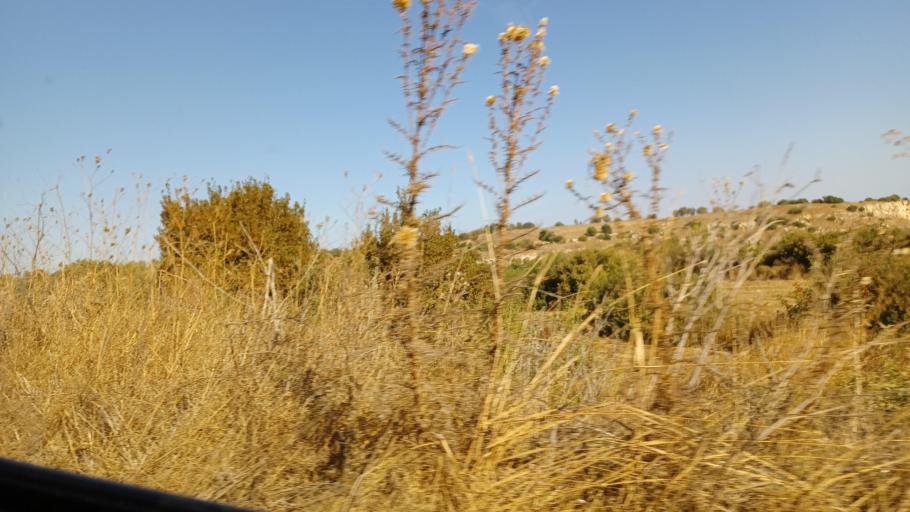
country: CY
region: Pafos
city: Polis
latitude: 34.9655
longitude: 32.4332
